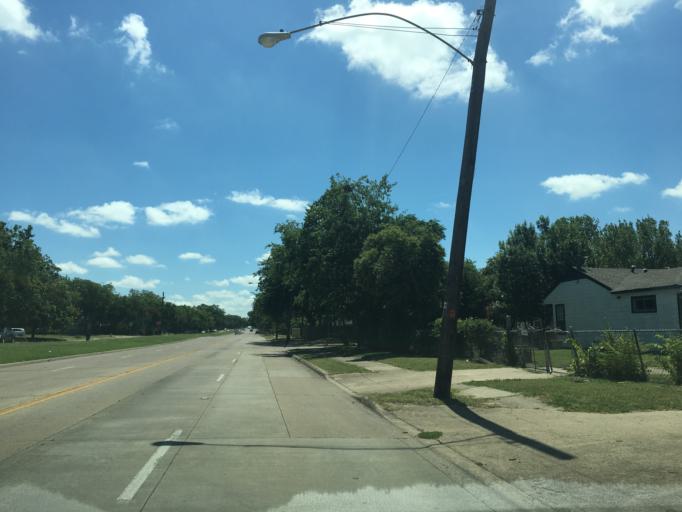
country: US
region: Texas
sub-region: Dallas County
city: Garland
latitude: 32.8429
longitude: -96.6788
